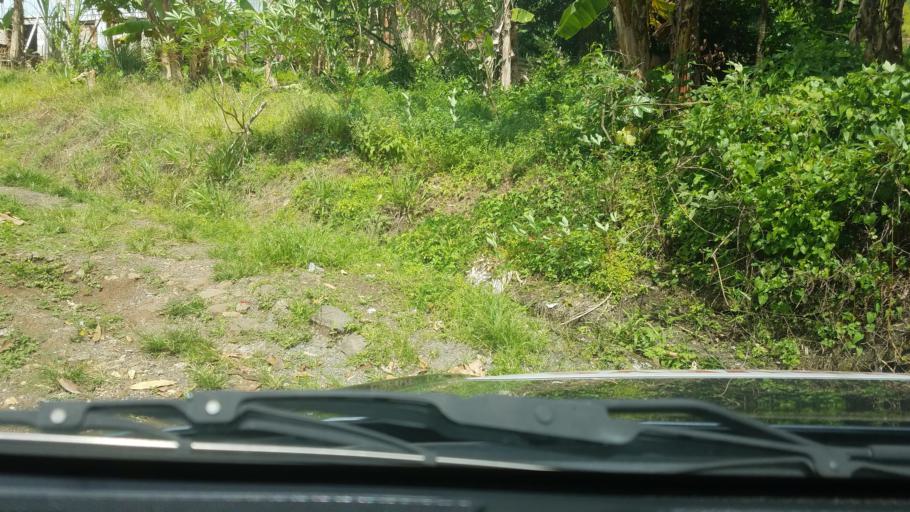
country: LC
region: Castries Quarter
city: Bisee
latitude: 14.0112
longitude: -60.9767
